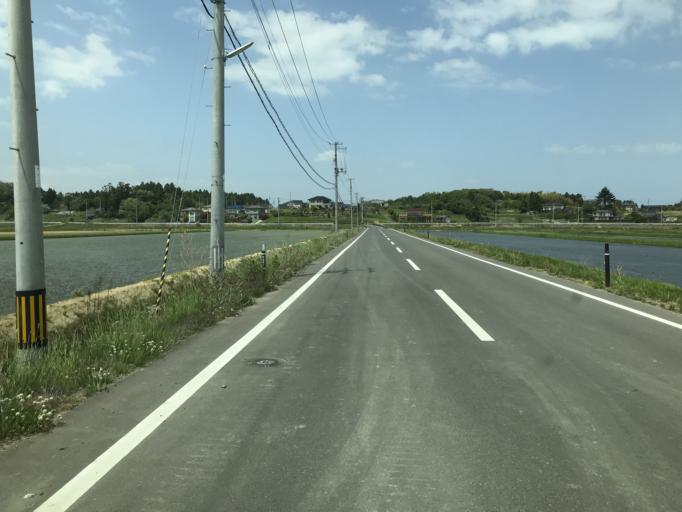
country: JP
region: Miyagi
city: Marumori
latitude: 37.8811
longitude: 140.9199
